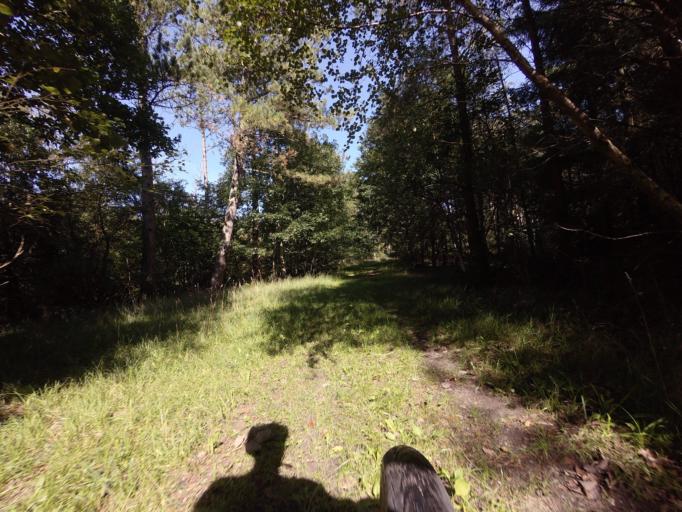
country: DK
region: North Denmark
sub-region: Hjorring Kommune
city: Hirtshals
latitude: 57.5859
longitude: 10.0032
